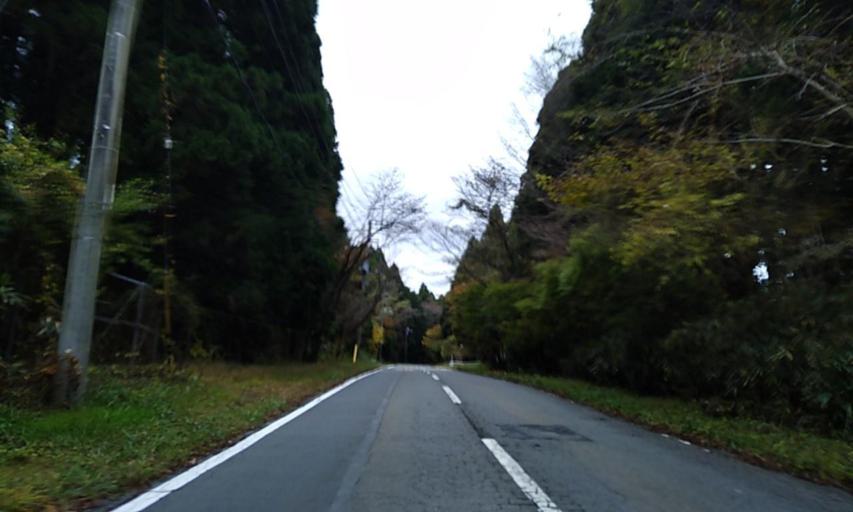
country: JP
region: Shizuoka
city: Gotemba
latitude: 35.2607
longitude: 138.8125
